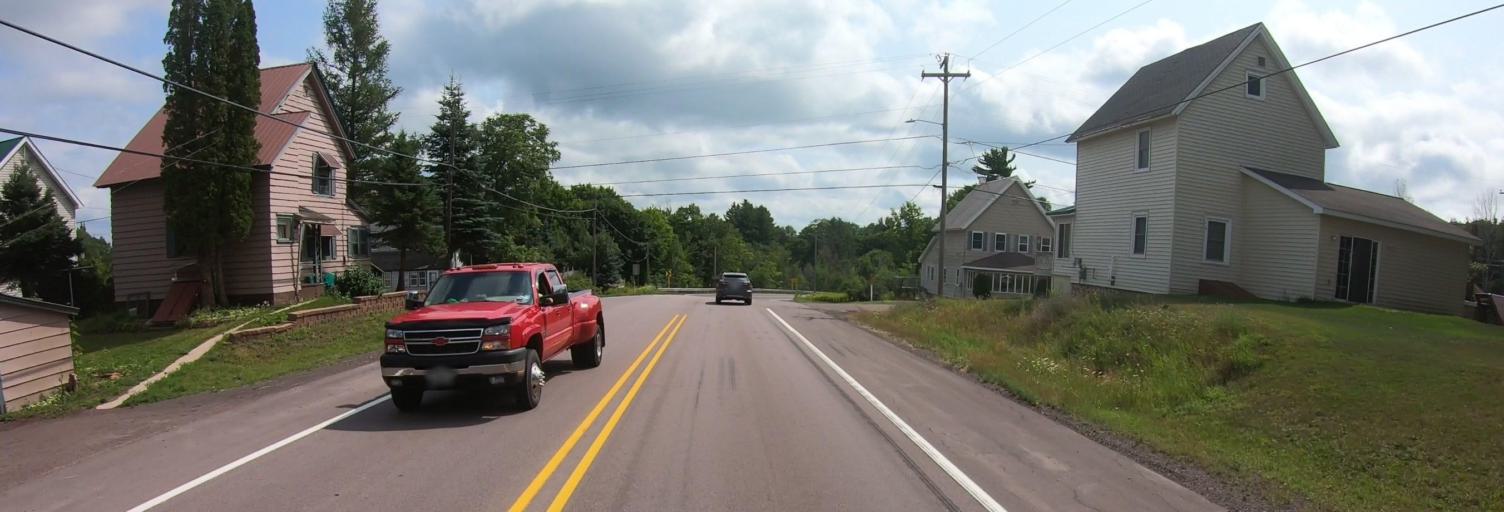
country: US
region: Michigan
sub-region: Houghton County
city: Hancock
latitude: 47.0408
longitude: -88.6725
